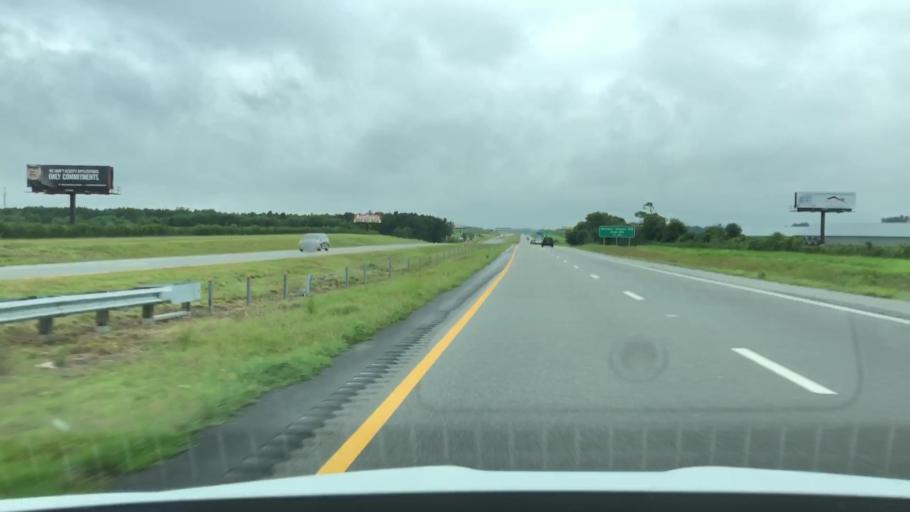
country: US
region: North Carolina
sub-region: Wayne County
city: Elroy
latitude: 35.4038
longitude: -77.8785
